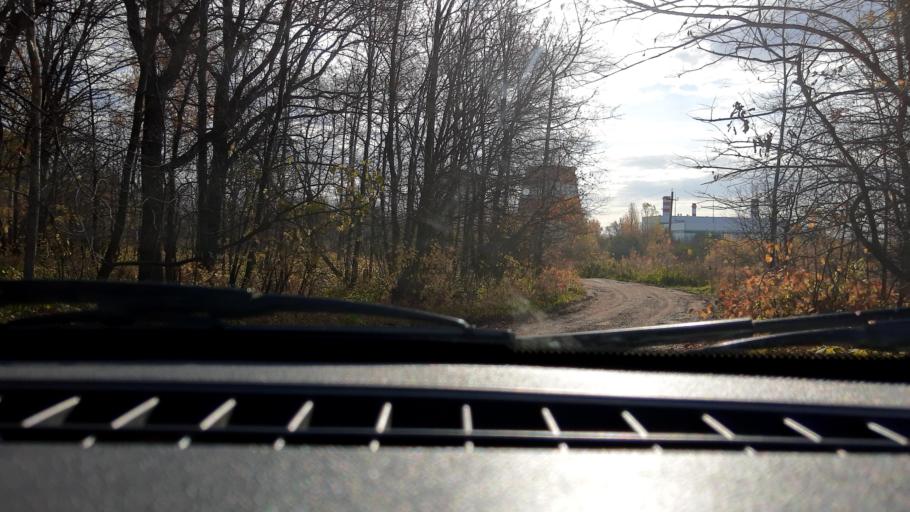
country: RU
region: Bashkortostan
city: Mikhaylovka
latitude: 54.8078
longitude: 55.8345
